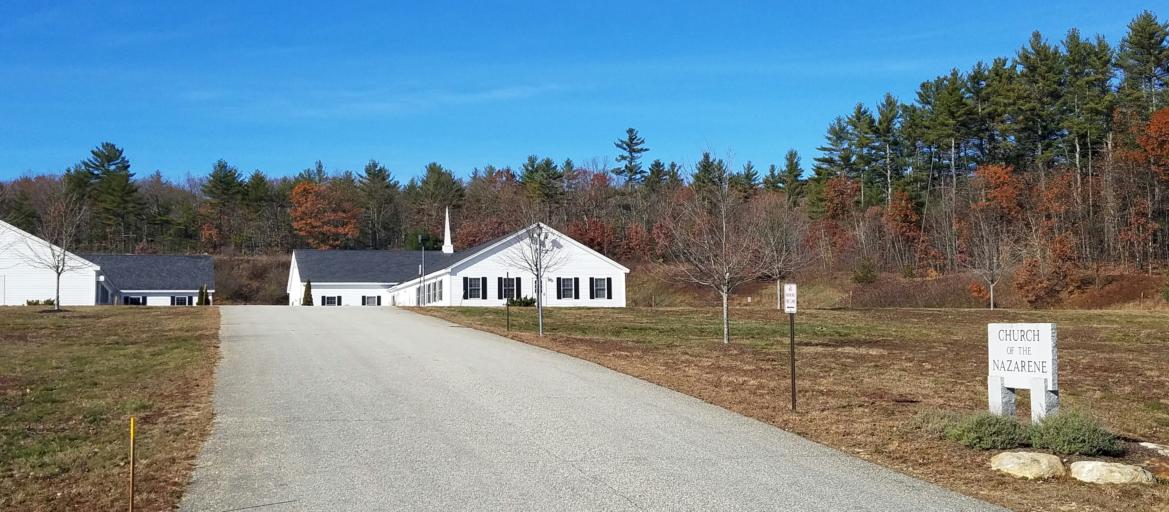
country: US
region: New Hampshire
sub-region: Merrimack County
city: Chichester
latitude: 43.2540
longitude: -71.4562
